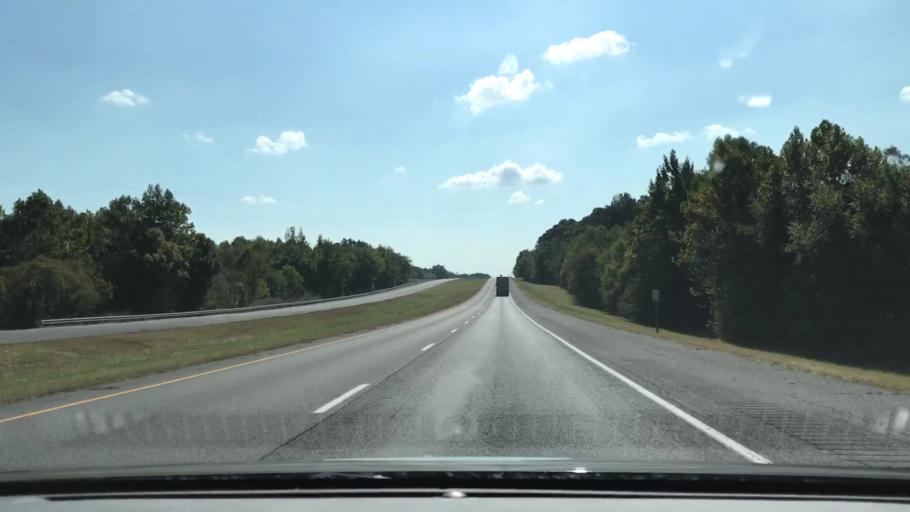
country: US
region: Kentucky
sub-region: Marshall County
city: Benton
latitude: 36.7746
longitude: -88.3188
